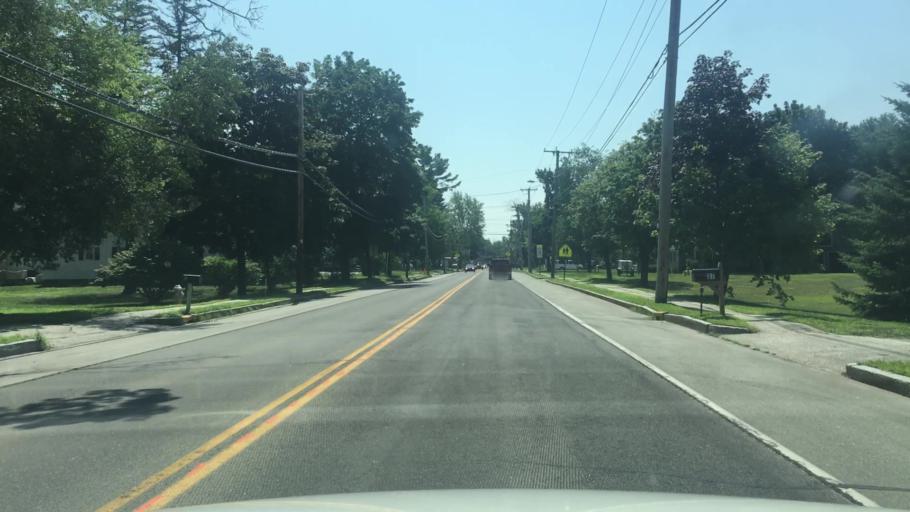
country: US
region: Maine
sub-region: Cumberland County
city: New Gloucester
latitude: 43.8896
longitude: -70.3342
